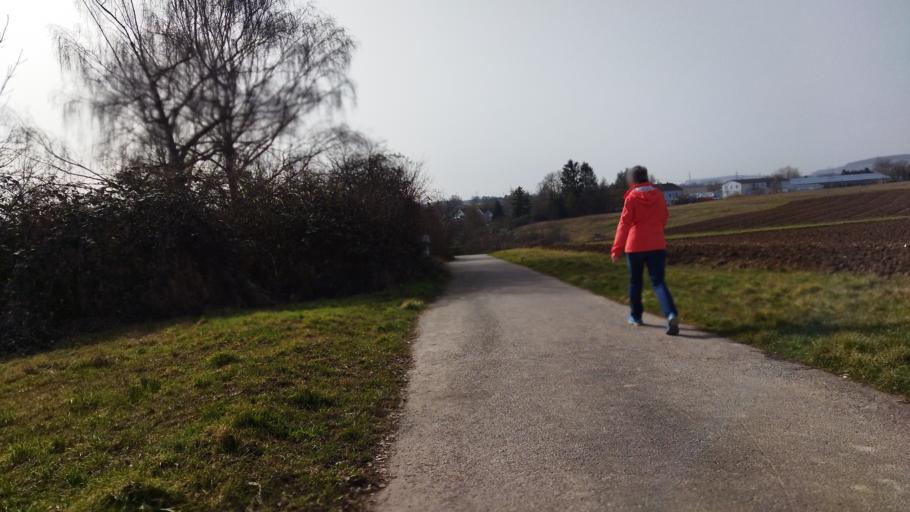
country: DE
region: Baden-Wuerttemberg
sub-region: Regierungsbezirk Stuttgart
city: Heilbronn
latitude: 49.1415
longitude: 9.1741
